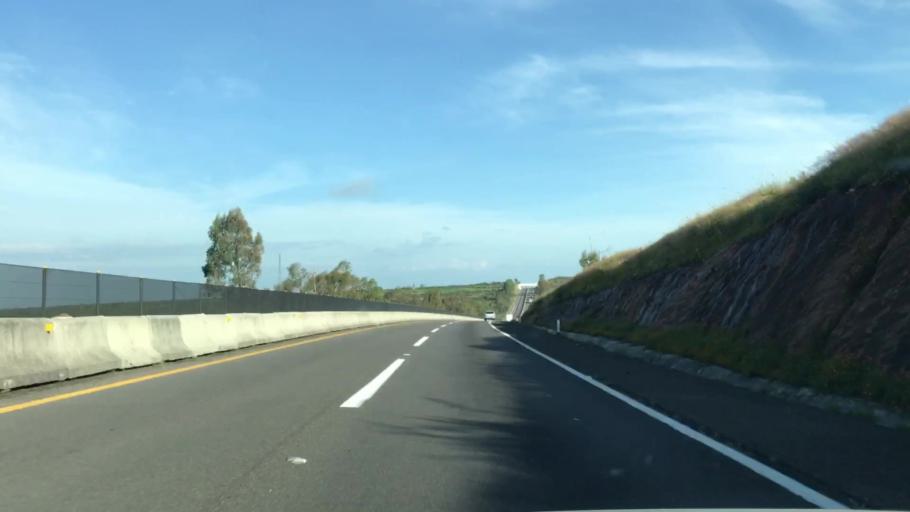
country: MX
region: Jalisco
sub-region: Lagos de Moreno
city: Cristeros [Fraccionamiento]
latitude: 21.3735
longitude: -102.1344
